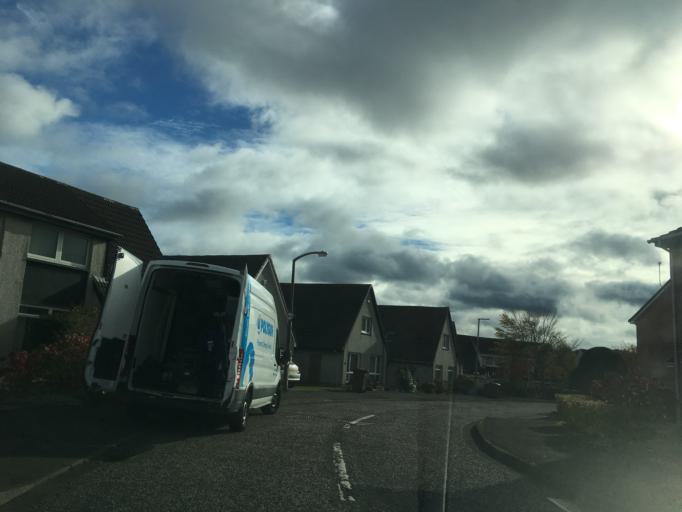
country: GB
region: Scotland
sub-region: Midlothian
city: Loanhead
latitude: 55.9060
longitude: -3.1700
